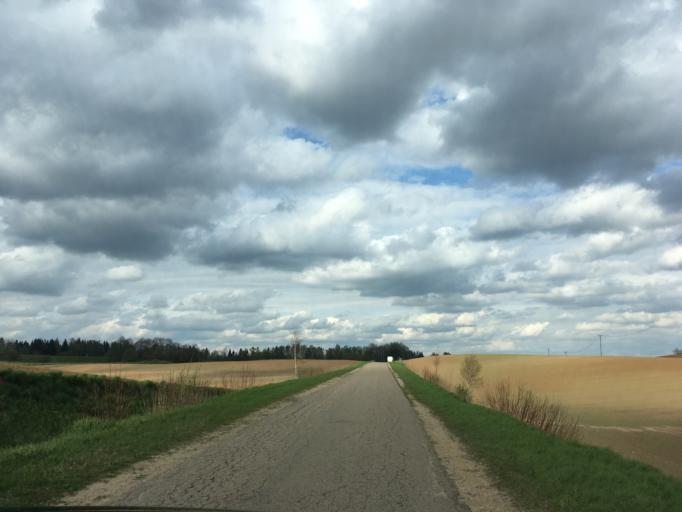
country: PL
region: Podlasie
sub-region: Suwalki
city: Suwalki
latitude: 54.3695
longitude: 22.9260
